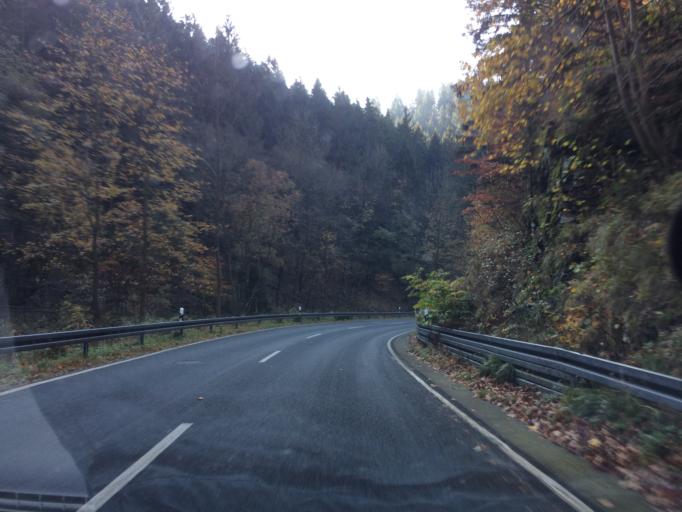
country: DE
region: Lower Saxony
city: Sankt Andreasberg
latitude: 51.7056
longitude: 10.5185
